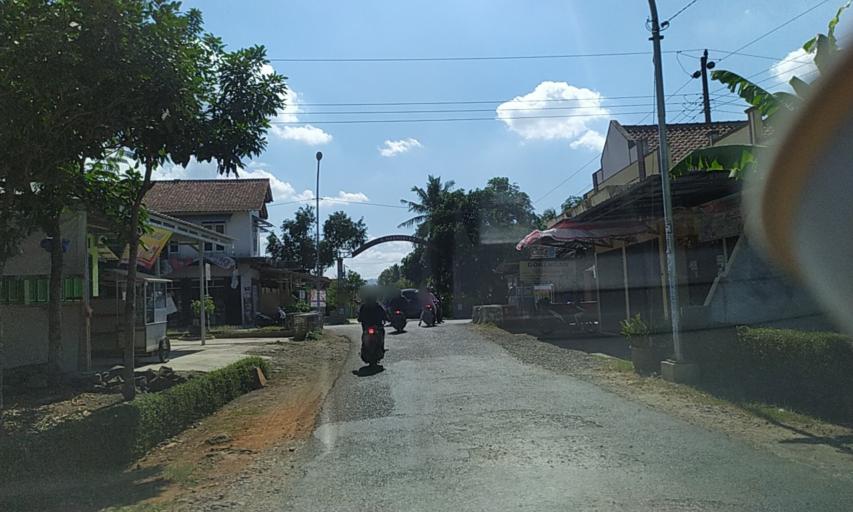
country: ID
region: Central Java
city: Rawaseser
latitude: -7.6010
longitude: 109.2469
